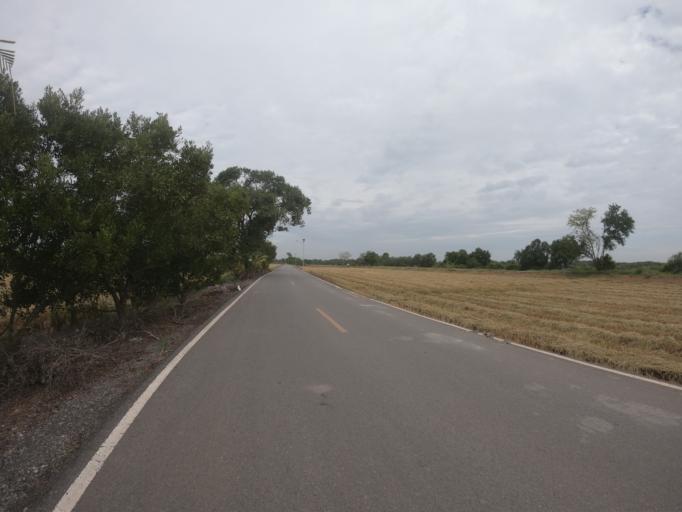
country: TH
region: Pathum Thani
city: Nong Suea
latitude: 14.0339
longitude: 100.8769
